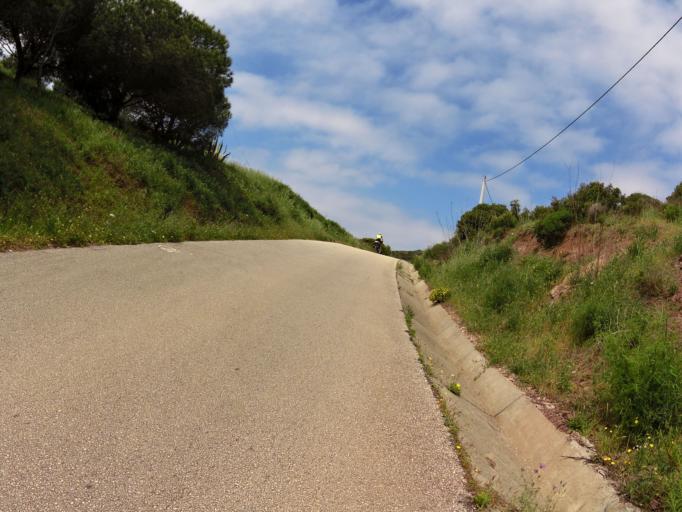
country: PT
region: Faro
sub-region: Vila do Bispo
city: Vila do Bispo
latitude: 37.0675
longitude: -8.8595
